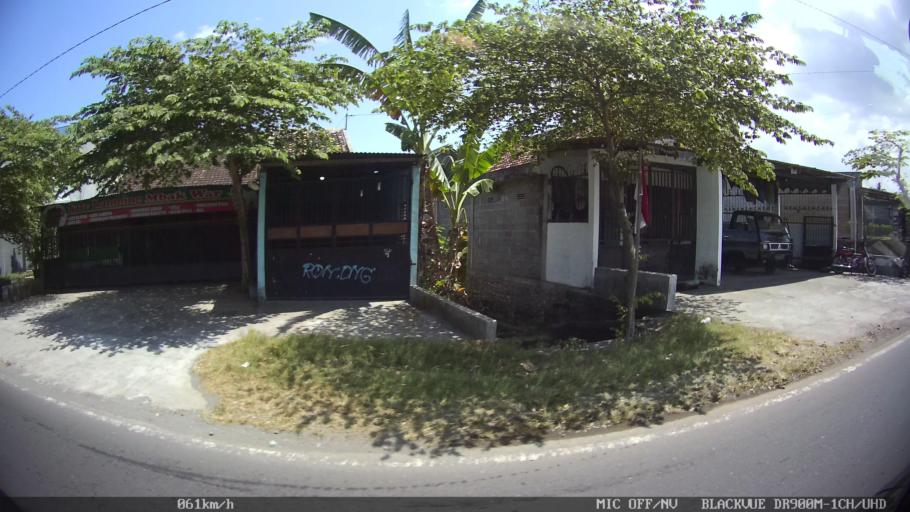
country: ID
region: Daerah Istimewa Yogyakarta
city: Pandak
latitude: -7.9155
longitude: 110.2857
